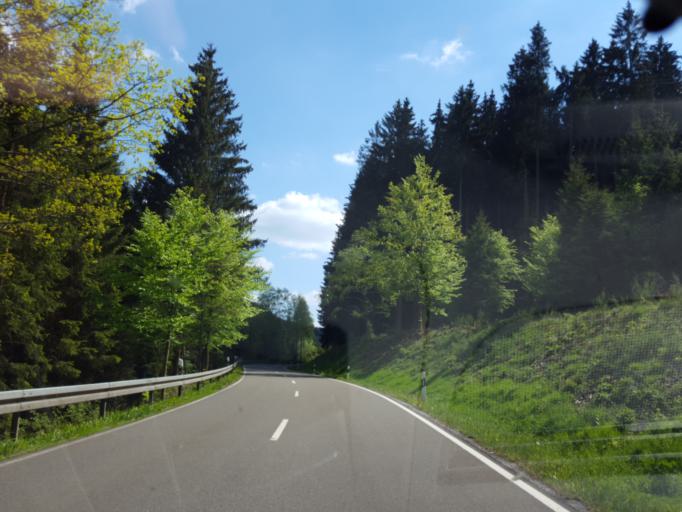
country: DE
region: North Rhine-Westphalia
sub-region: Regierungsbezirk Arnsberg
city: Olsberg
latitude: 51.2994
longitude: 8.4465
